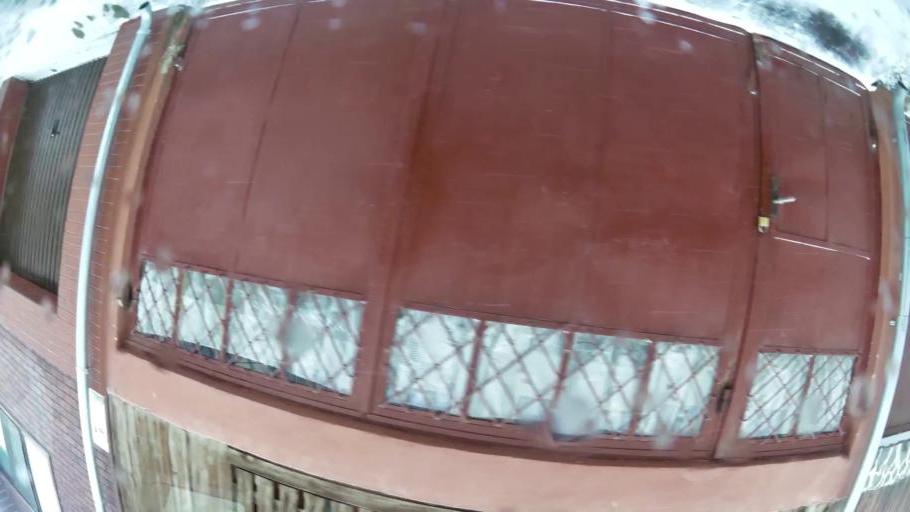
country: RO
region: Dambovita
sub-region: Municipiul Targoviste
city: Targoviste
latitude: 44.9134
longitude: 25.4738
